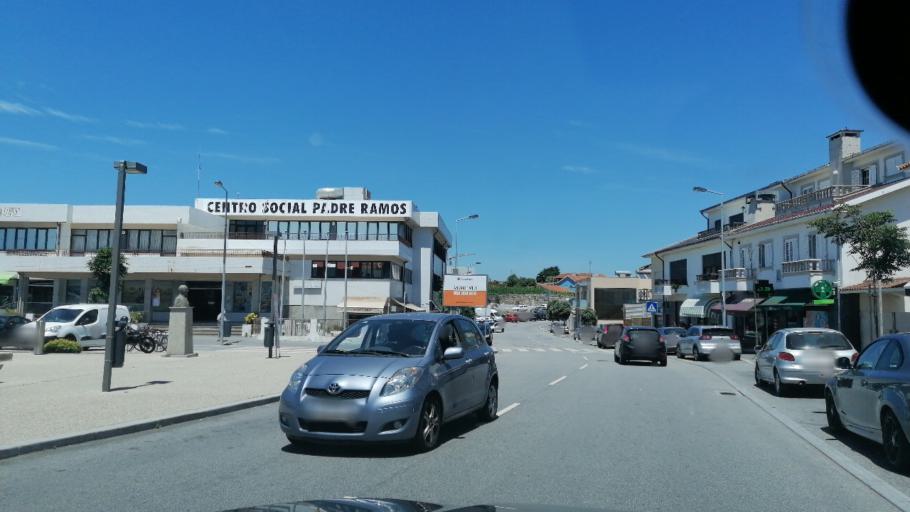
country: PT
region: Porto
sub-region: Matosinhos
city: Lavra
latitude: 41.2588
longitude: -8.7177
